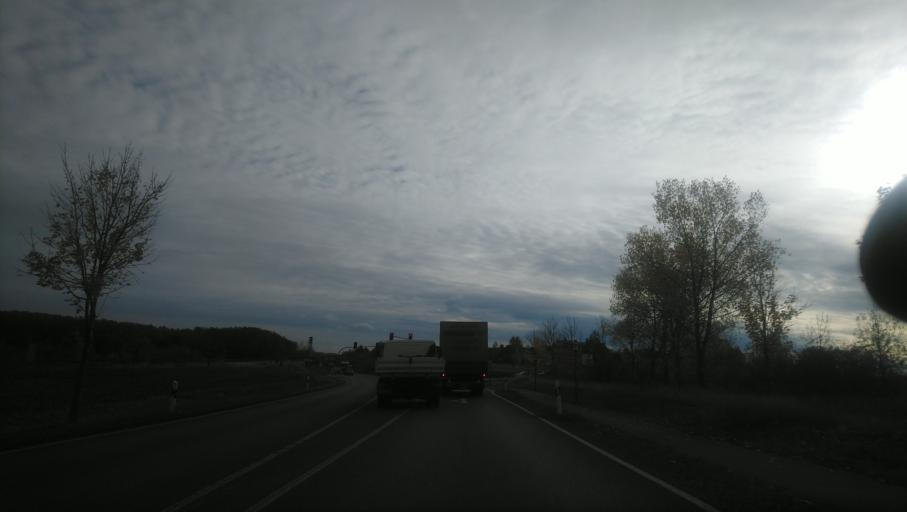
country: DE
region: Saxony
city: Wilkau-Hasslau
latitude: 50.6971
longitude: 12.5288
